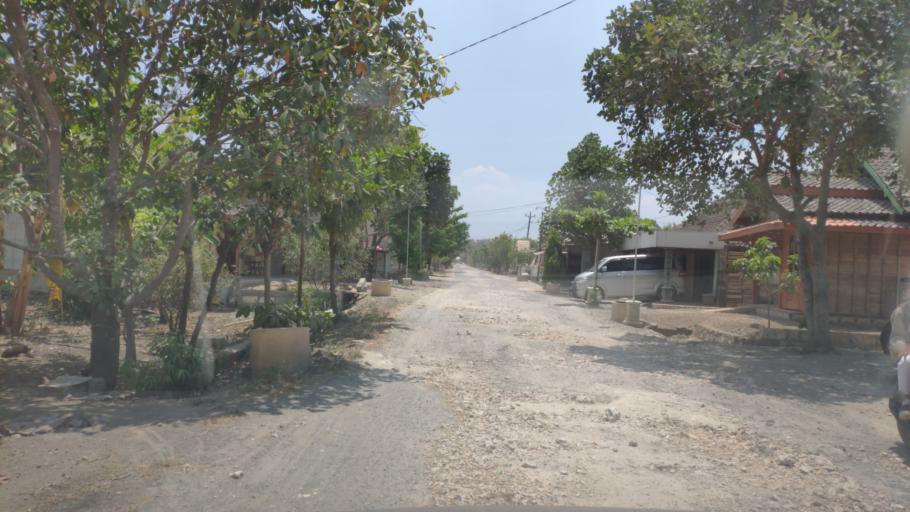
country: ID
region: Central Java
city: Kemantren
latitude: -7.2105
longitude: 111.5219
